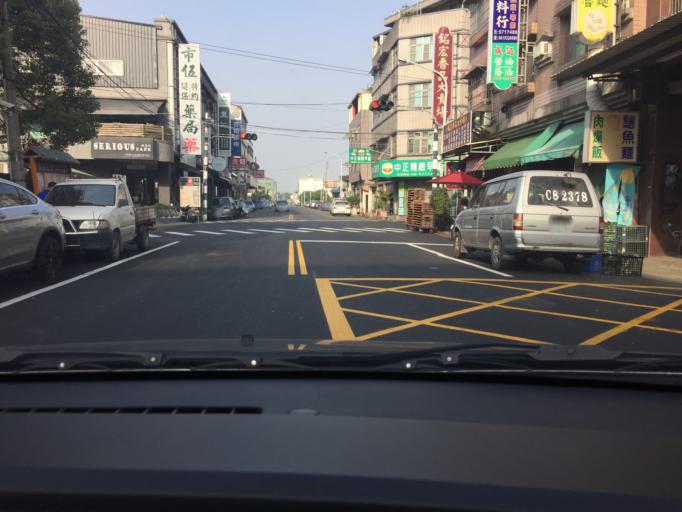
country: TW
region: Taiwan
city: Xinying
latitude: 23.1861
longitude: 120.2496
